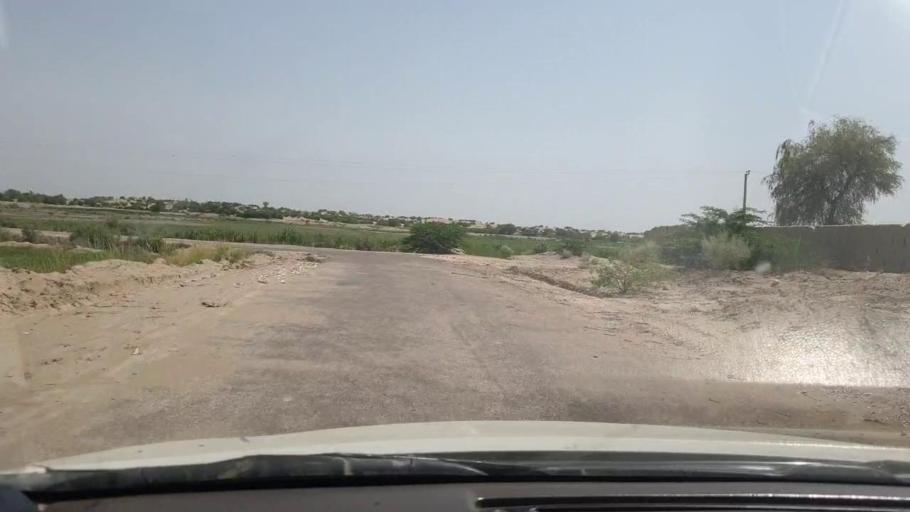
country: PK
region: Sindh
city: Rohri
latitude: 27.4831
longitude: 69.0551
